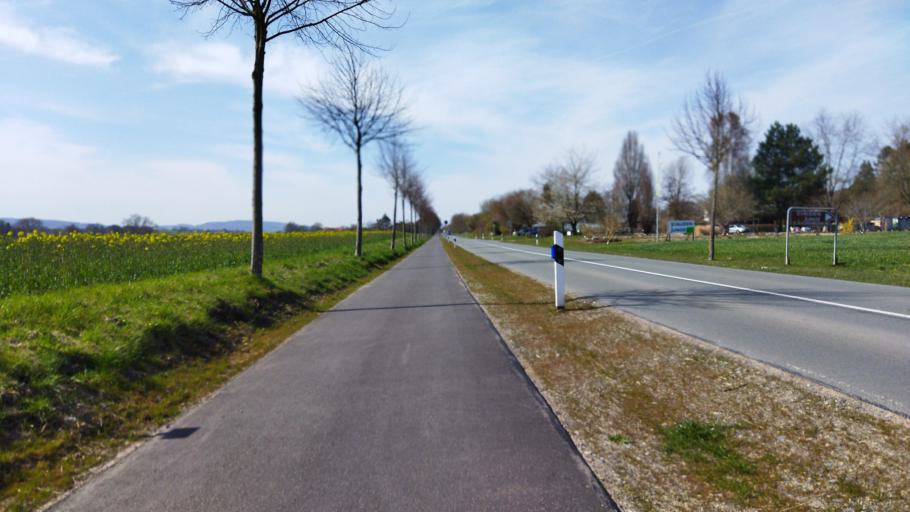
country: DE
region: Lower Saxony
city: Hameln
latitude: 52.1208
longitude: 9.3193
